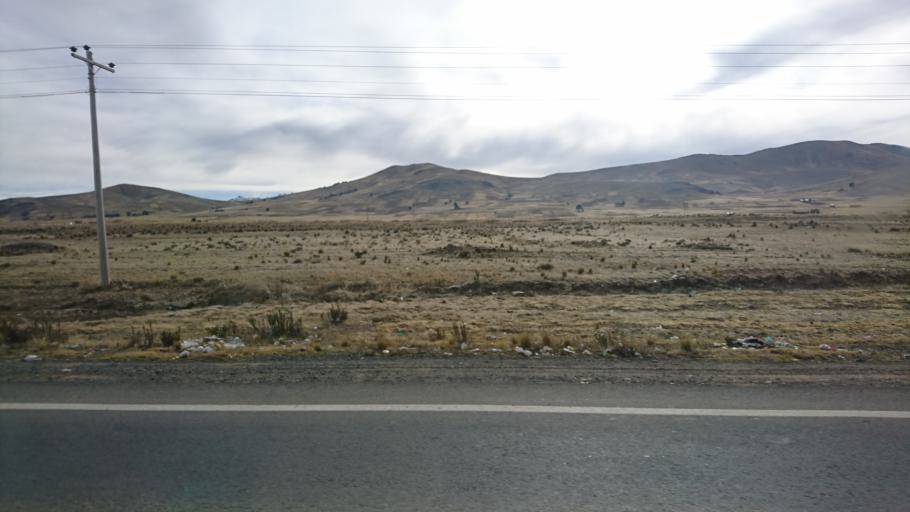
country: BO
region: La Paz
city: Batallas
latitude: -16.3826
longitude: -68.3748
